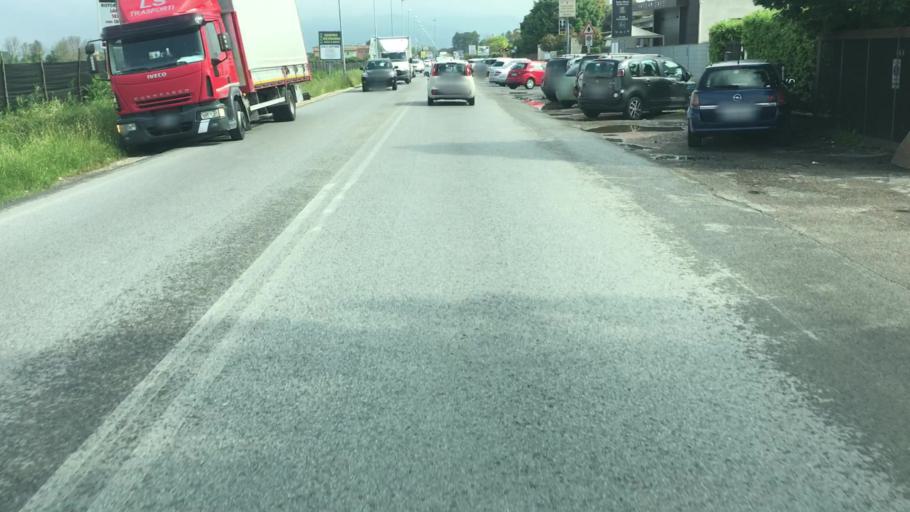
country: IT
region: Tuscany
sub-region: Province of Florence
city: San Mauro
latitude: 43.8085
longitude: 11.1178
